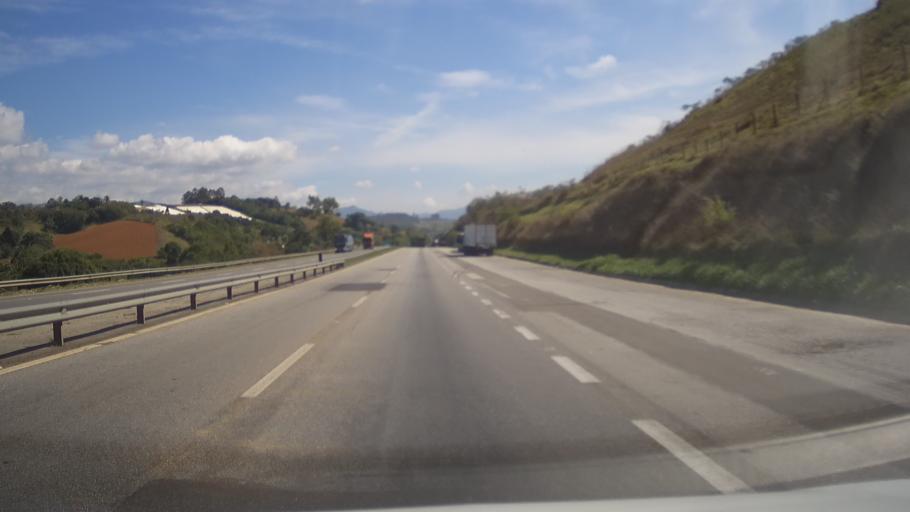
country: BR
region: Minas Gerais
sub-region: Cambui
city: Cambui
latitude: -22.5626
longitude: -46.0407
